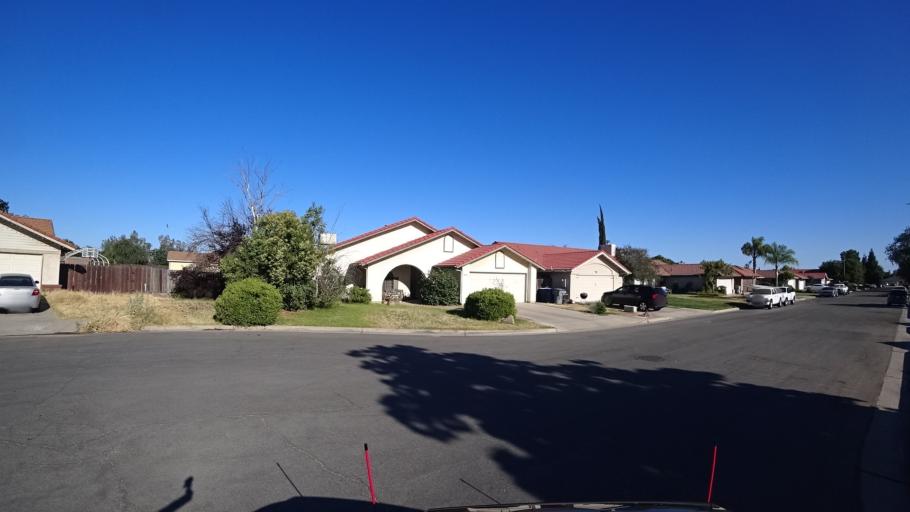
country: US
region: California
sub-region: Fresno County
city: West Park
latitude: 36.7831
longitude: -119.8664
